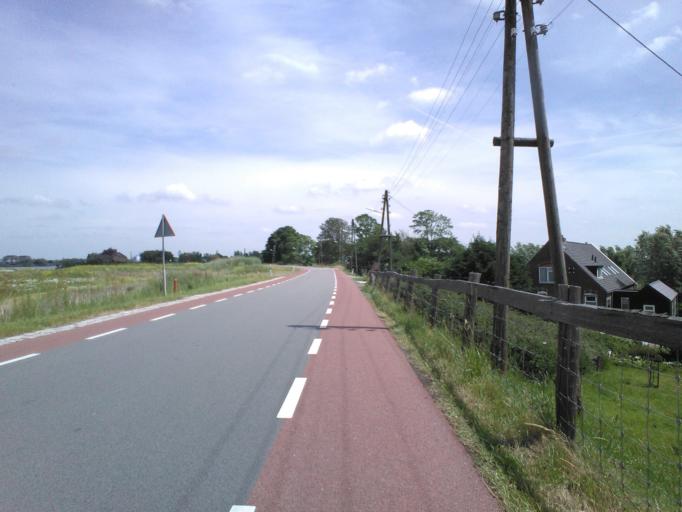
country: NL
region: South Holland
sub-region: Gemeente Gouda
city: Bloemendaal
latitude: 51.9757
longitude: 4.6578
